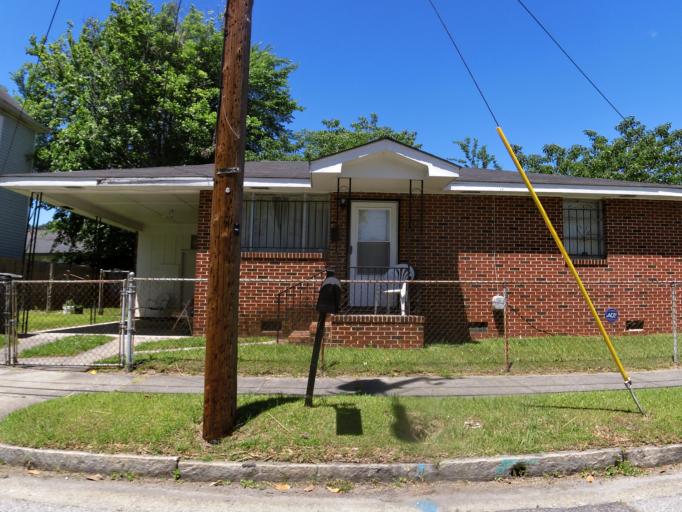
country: US
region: Georgia
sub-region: Richmond County
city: Augusta
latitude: 33.4682
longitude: -81.9755
